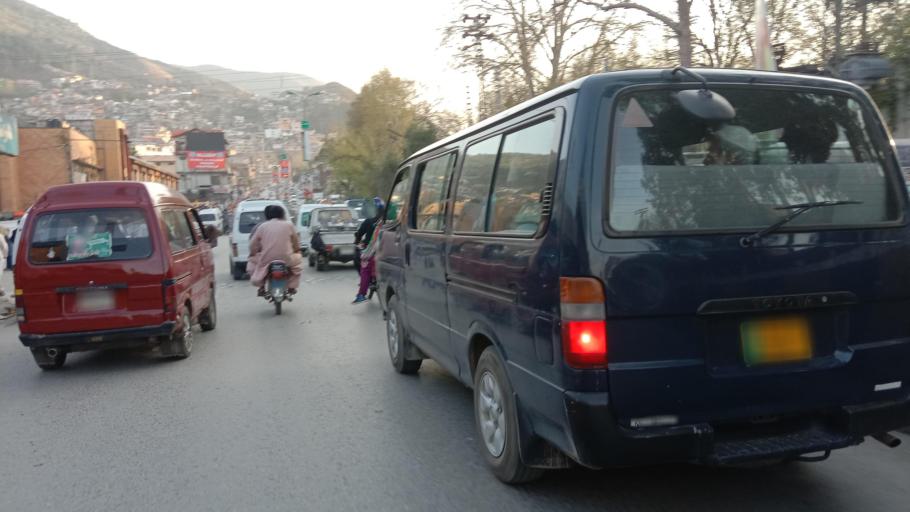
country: PK
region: Khyber Pakhtunkhwa
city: Abbottabad
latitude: 34.1453
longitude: 73.2152
